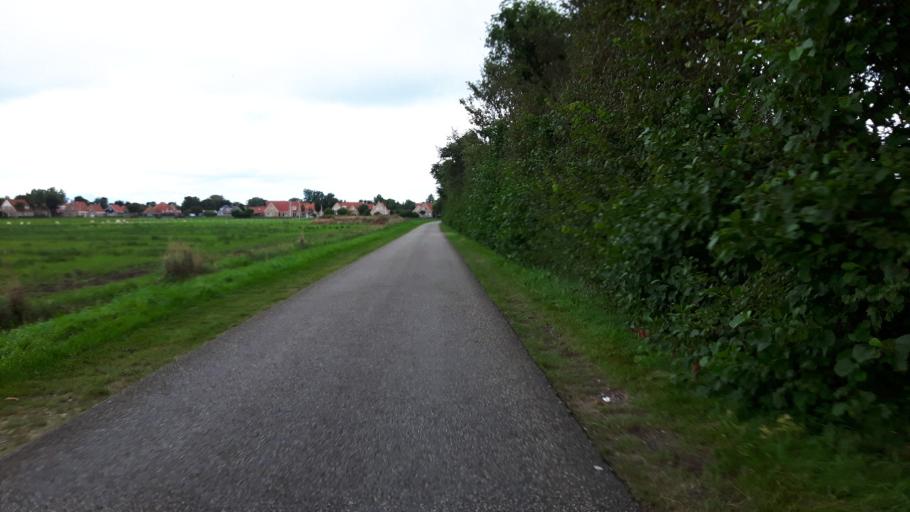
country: NL
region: Friesland
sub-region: Gemeente Ameland
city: Hollum
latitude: 53.4422
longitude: 5.6482
